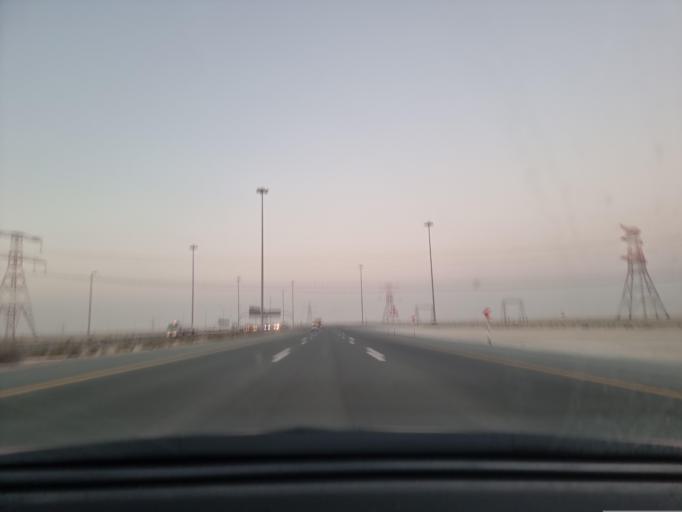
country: AE
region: Abu Dhabi
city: Abu Dhabi
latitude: 24.4242
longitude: 54.7649
